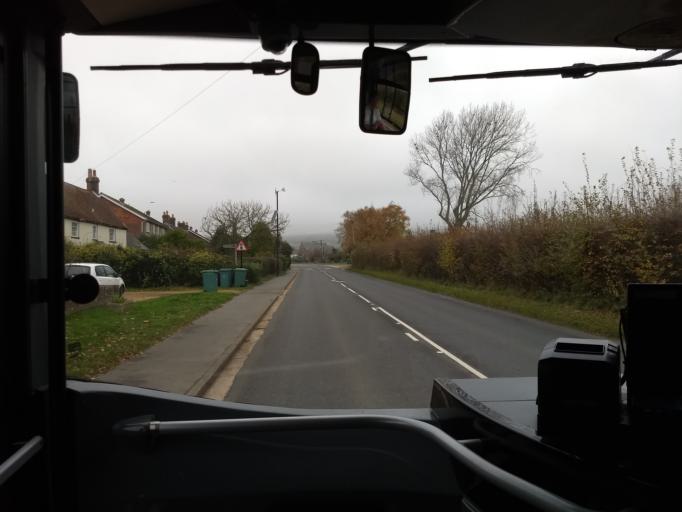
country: GB
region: England
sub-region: Isle of Wight
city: Newchurch
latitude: 50.6692
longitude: -1.2327
